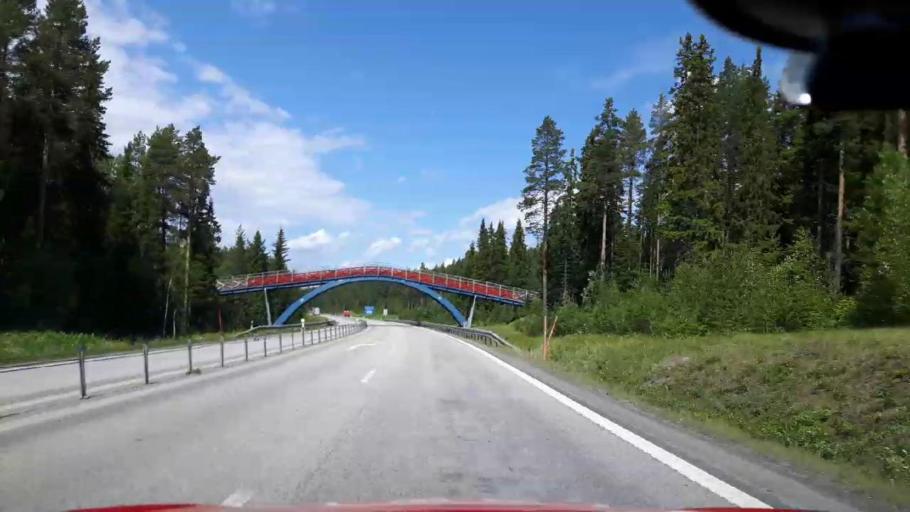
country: SE
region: Jaemtland
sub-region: OEstersunds Kommun
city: Ostersund
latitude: 63.1926
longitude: 14.6899
